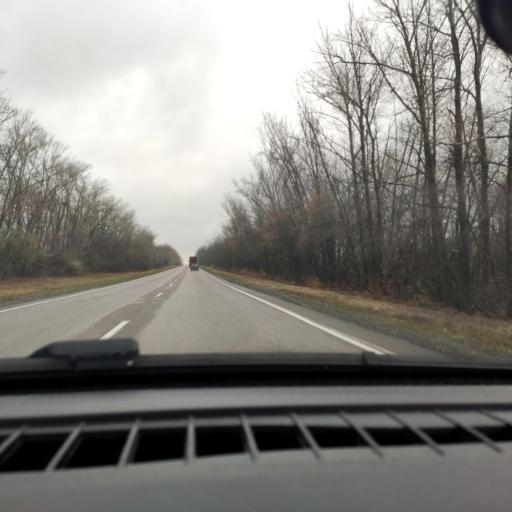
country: RU
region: Voronezj
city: Ostrogozhsk
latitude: 51.0075
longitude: 38.9983
